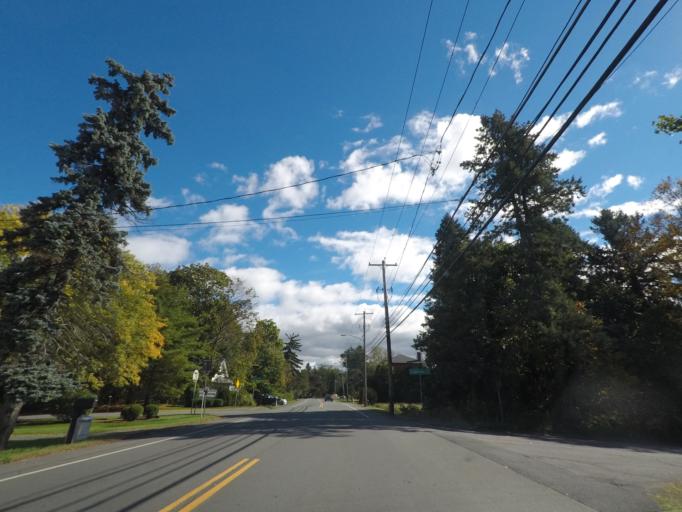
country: US
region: New York
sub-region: Albany County
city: Watervliet
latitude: 42.7278
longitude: -73.7330
